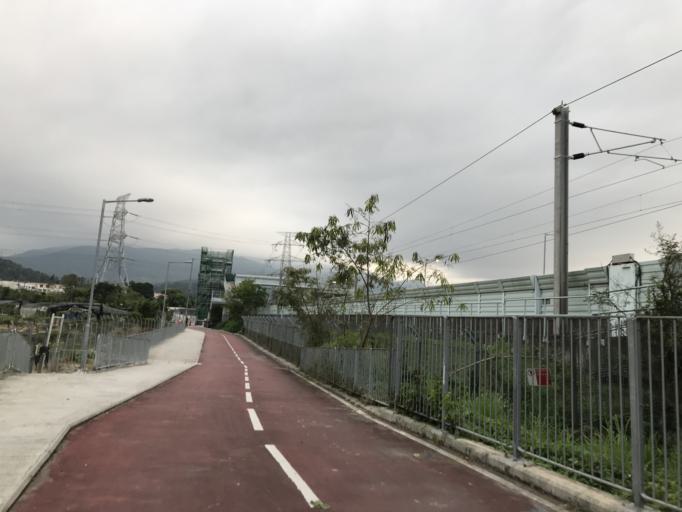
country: HK
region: Tai Po
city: Tai Po
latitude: 22.4697
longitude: 114.1534
